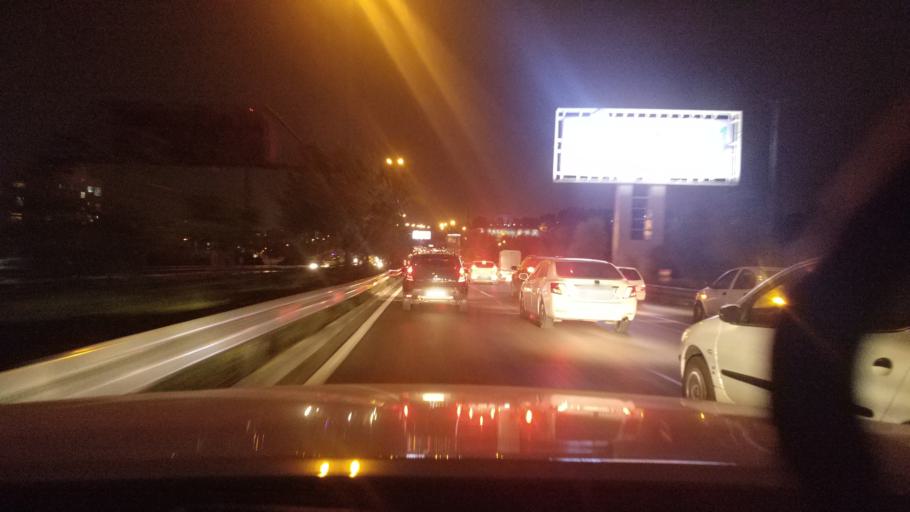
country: IR
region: Tehran
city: Tehran
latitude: 35.7401
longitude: 51.3733
